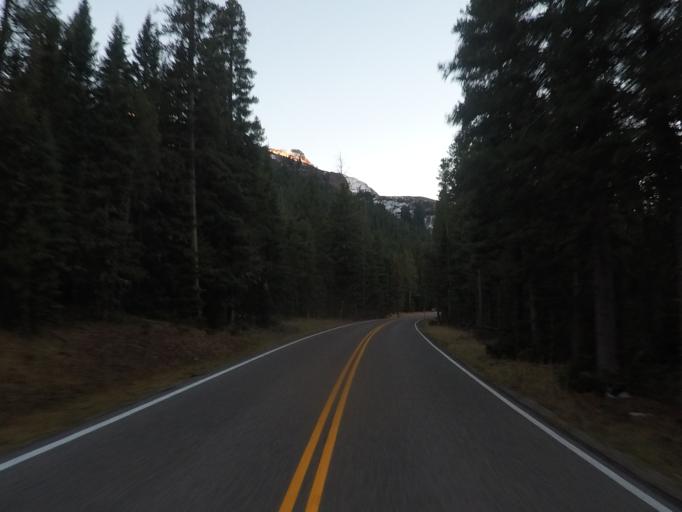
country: US
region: Montana
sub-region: Stillwater County
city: Absarokee
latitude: 44.9895
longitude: -110.0562
